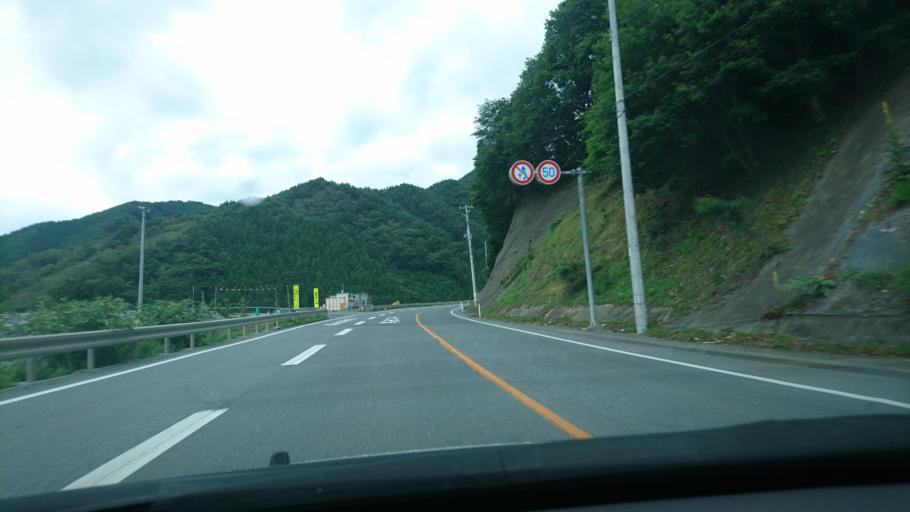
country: JP
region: Iwate
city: Kamaishi
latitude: 39.2162
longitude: 141.8741
